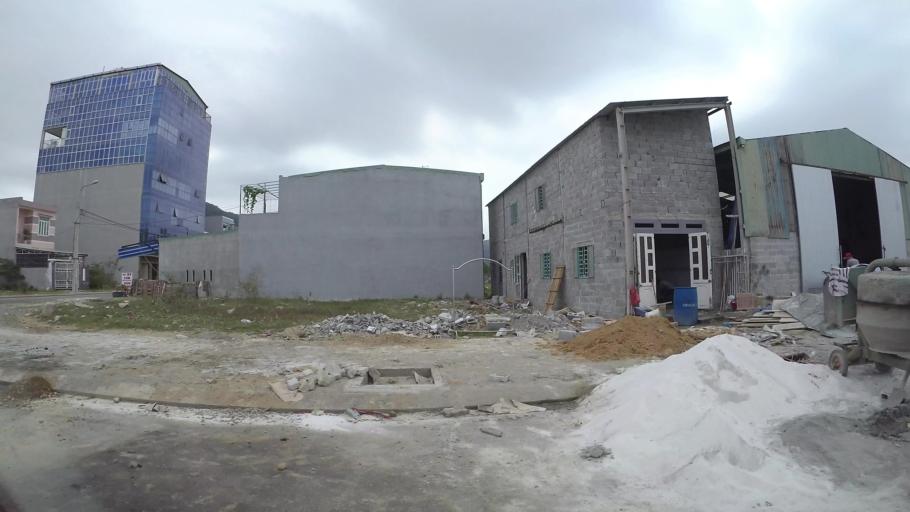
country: VN
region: Da Nang
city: Lien Chieu
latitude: 16.0489
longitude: 108.1665
